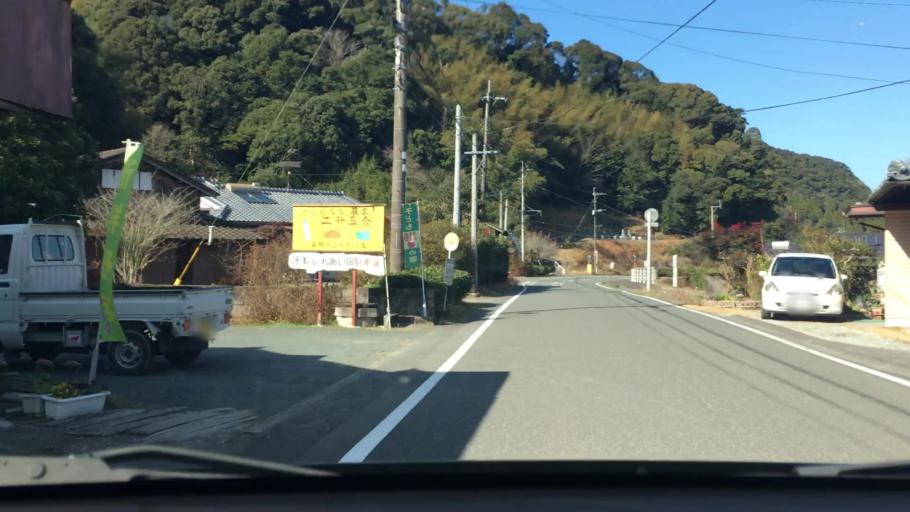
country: JP
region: Kagoshima
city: Ijuin
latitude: 31.7418
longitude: 130.4098
